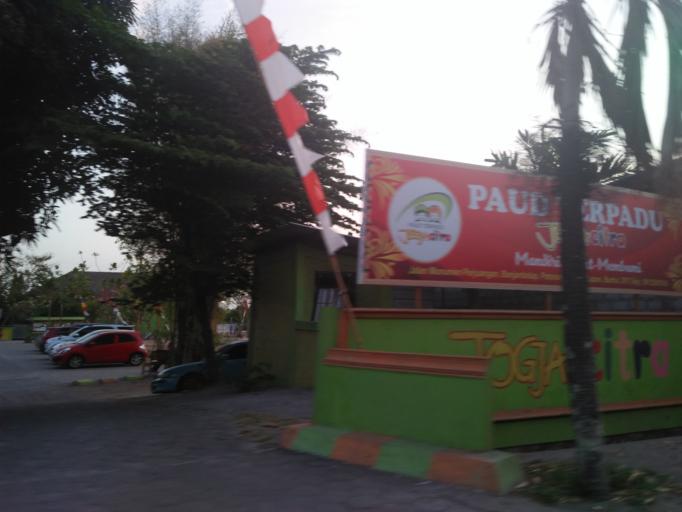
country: ID
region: Daerah Istimewa Yogyakarta
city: Sewon
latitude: -7.8480
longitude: 110.4100
